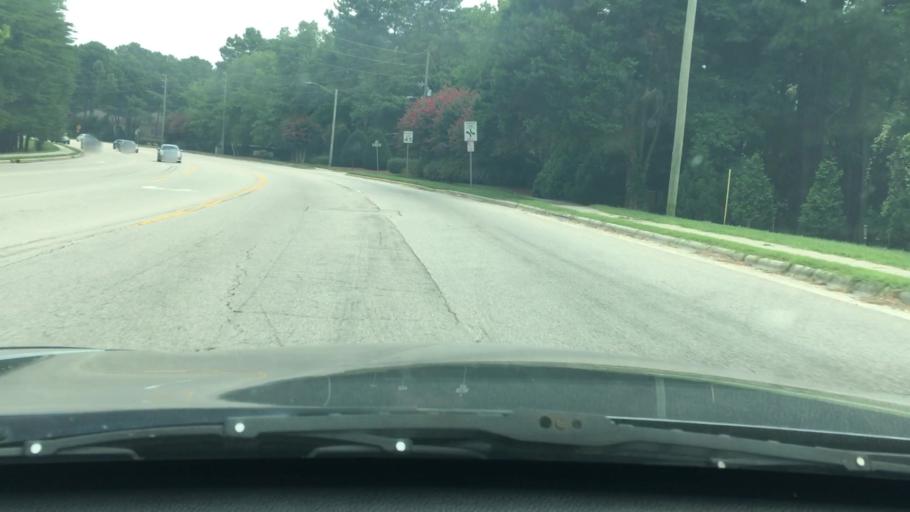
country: US
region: North Carolina
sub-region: Wake County
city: West Raleigh
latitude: 35.8267
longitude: -78.7107
